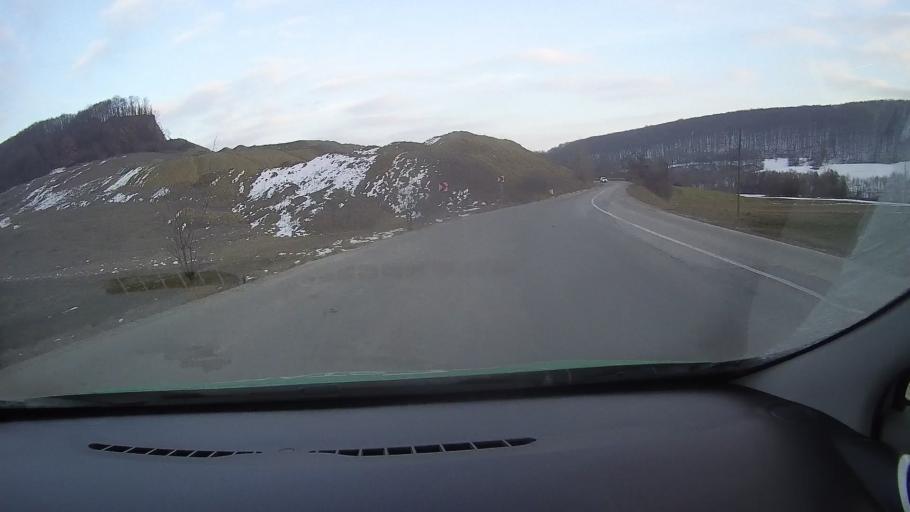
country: RO
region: Harghita
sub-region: Comuna Lupeni
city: Lupeni
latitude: 46.3597
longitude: 25.1890
